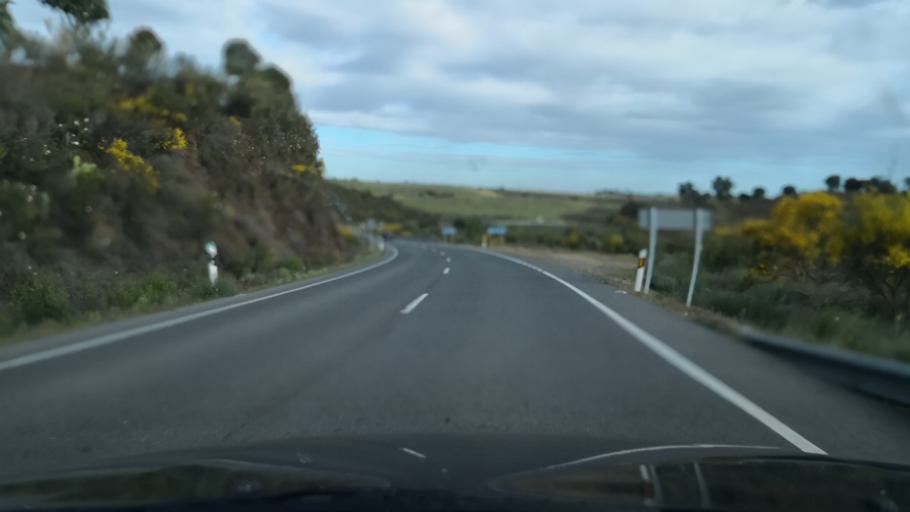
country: ES
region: Extremadura
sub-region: Provincia de Caceres
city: Perales del Puerto
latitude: 40.1249
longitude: -6.6781
